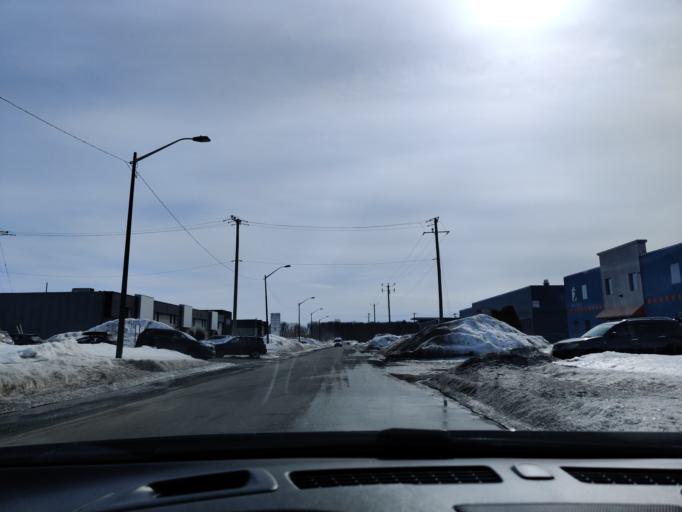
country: CA
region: Quebec
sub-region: Laurentides
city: Saint-Jerome
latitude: 45.7572
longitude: -73.9935
